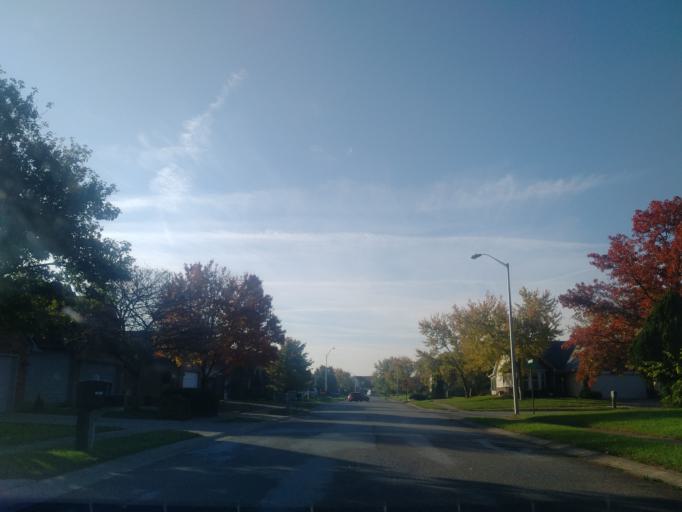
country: US
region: Indiana
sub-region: Marion County
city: Cumberland
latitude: 39.7905
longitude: -85.9890
